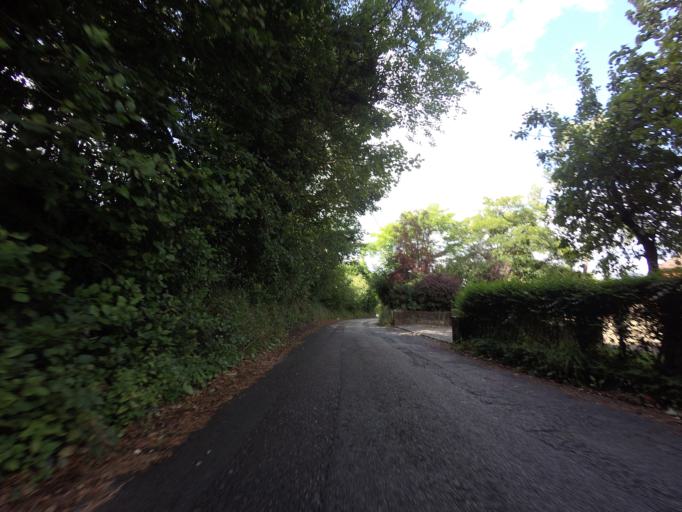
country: GB
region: England
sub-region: Kent
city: Borough Green
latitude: 51.2773
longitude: 0.2748
